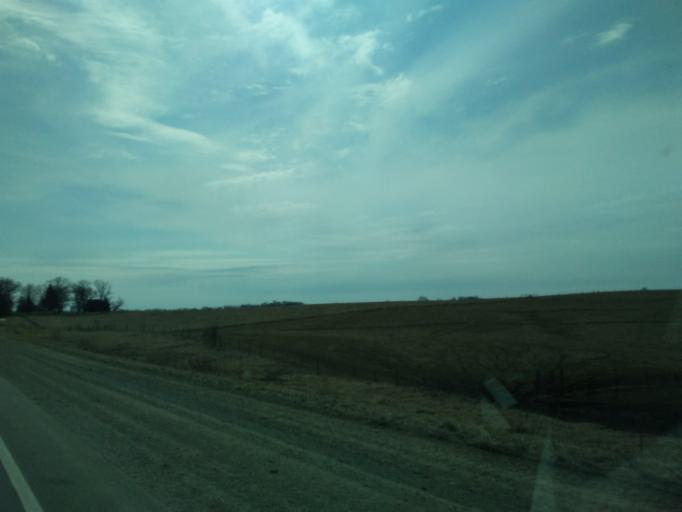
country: US
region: Iowa
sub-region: Winneshiek County
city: Decorah
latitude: 43.4261
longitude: -91.8593
